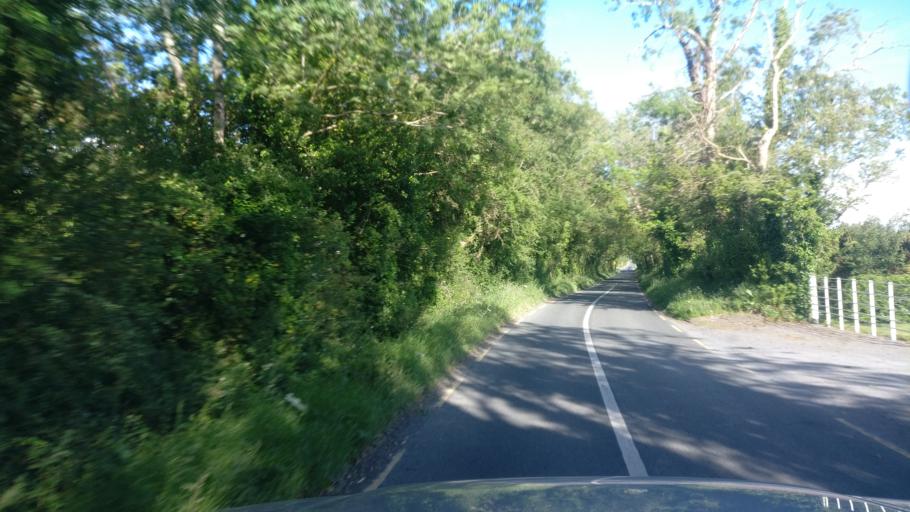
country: IE
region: Connaught
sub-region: County Galway
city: Ballinasloe
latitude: 53.2228
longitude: -8.1981
